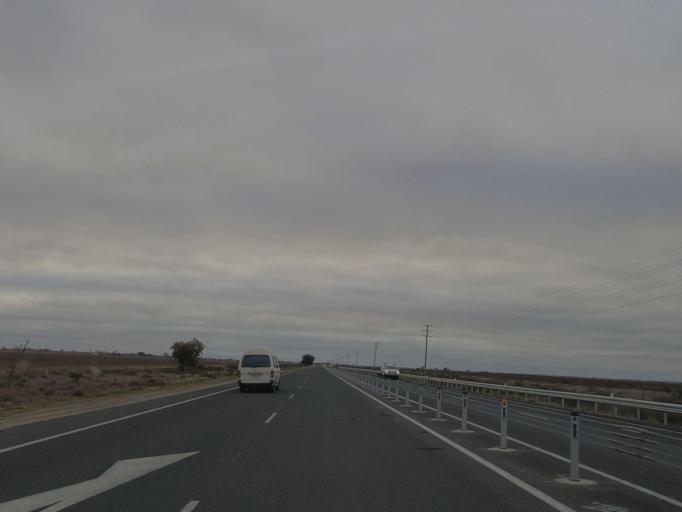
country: AU
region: Victoria
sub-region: Swan Hill
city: Swan Hill
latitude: -35.5081
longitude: 143.7224
